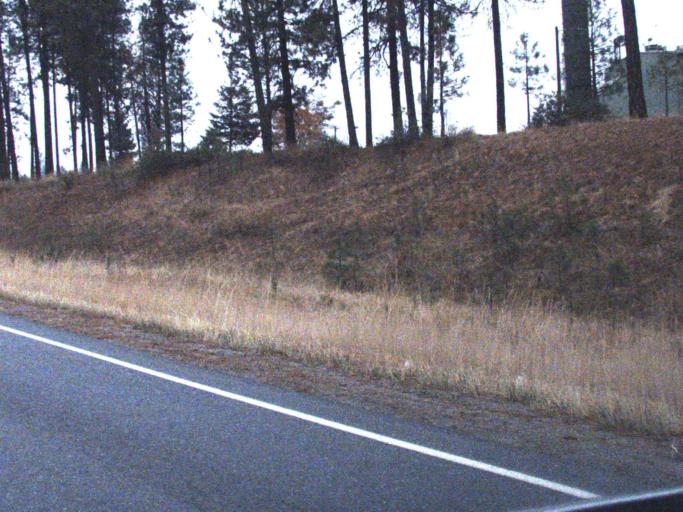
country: US
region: Washington
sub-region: Stevens County
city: Kettle Falls
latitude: 48.6212
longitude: -118.1093
